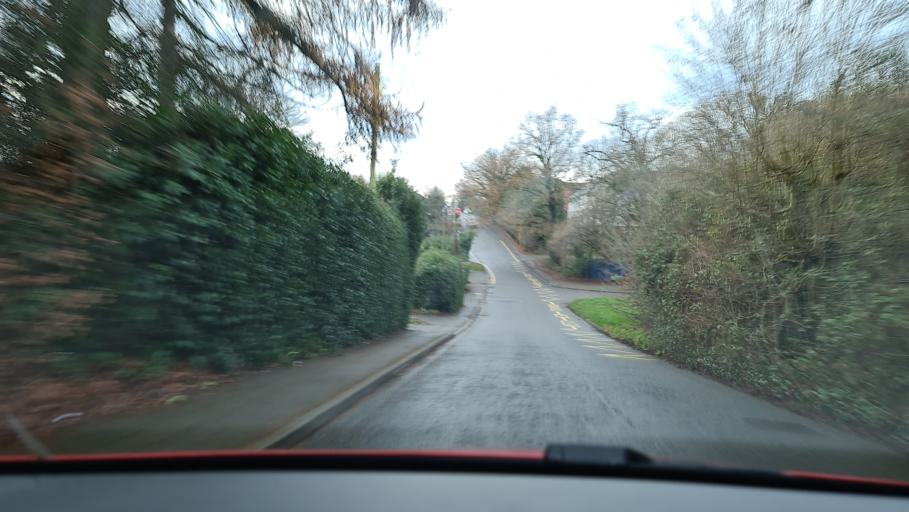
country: GB
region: England
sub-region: Buckinghamshire
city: Little Chalfont
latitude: 51.6725
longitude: -0.5716
